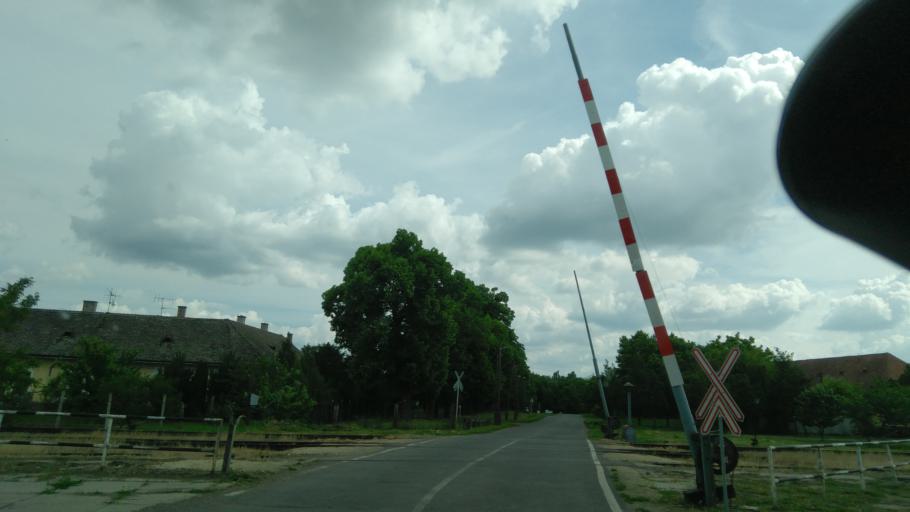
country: HU
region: Bekes
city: Mezohegyes
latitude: 46.3128
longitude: 20.8234
